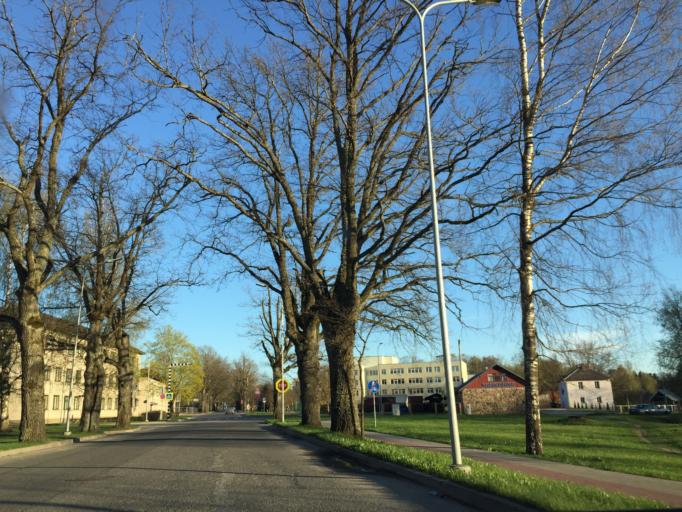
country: LV
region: Valmieras Rajons
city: Valmiera
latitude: 57.5482
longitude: 25.4217
